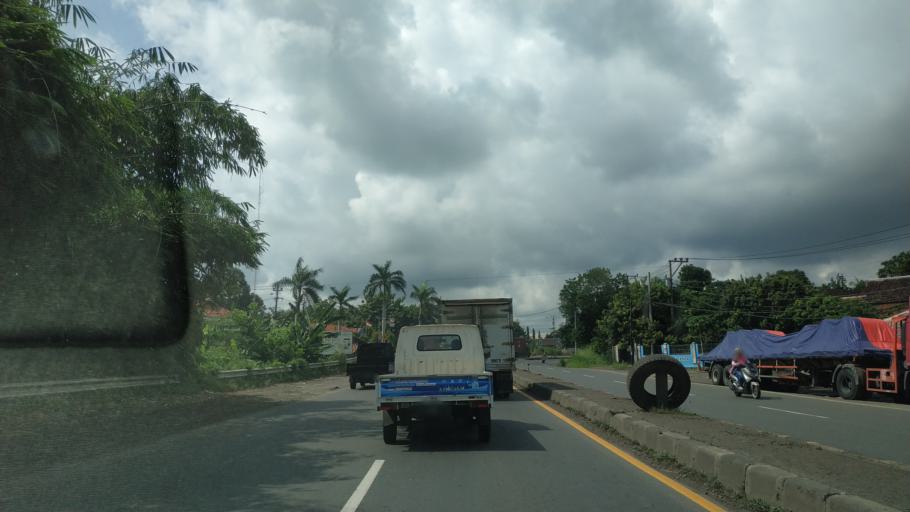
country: ID
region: Central Java
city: Pekalongan
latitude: -6.9248
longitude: 109.7624
